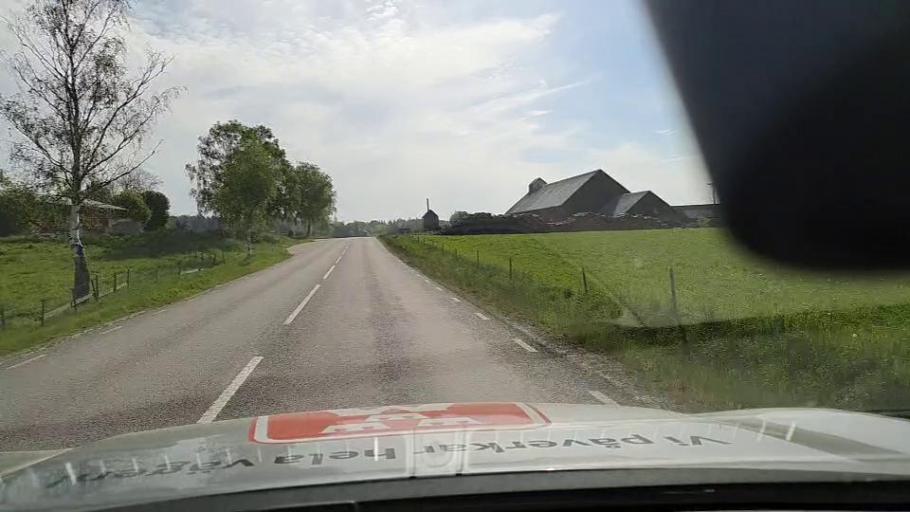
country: SE
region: Soedermanland
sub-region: Eskilstuna Kommun
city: Eskilstuna
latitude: 59.3185
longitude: 16.5515
